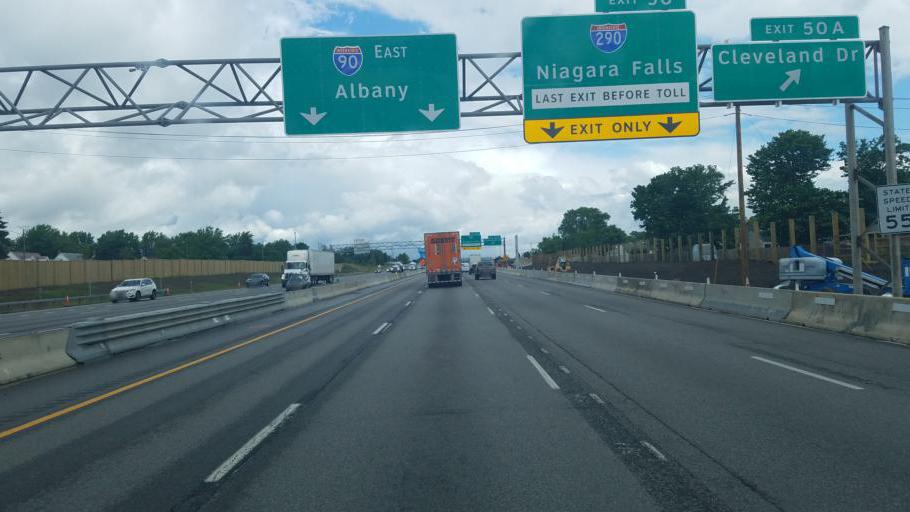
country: US
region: New York
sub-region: Erie County
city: Cheektowaga
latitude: 42.9392
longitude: -78.7662
